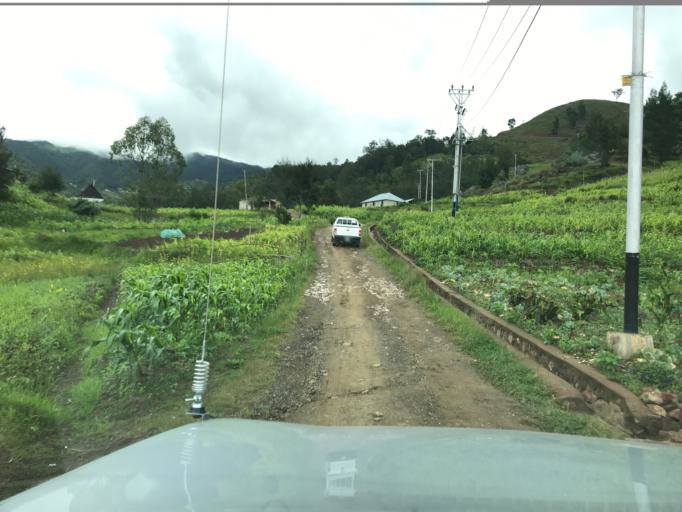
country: TL
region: Aileu
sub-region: Aileu Villa
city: Aileu
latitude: -8.8600
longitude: 125.5678
